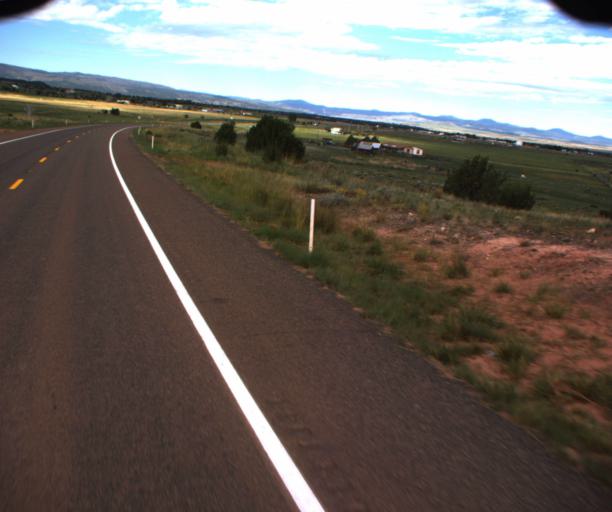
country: US
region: Arizona
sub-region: Apache County
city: Springerville
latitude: 34.1350
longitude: -109.2354
